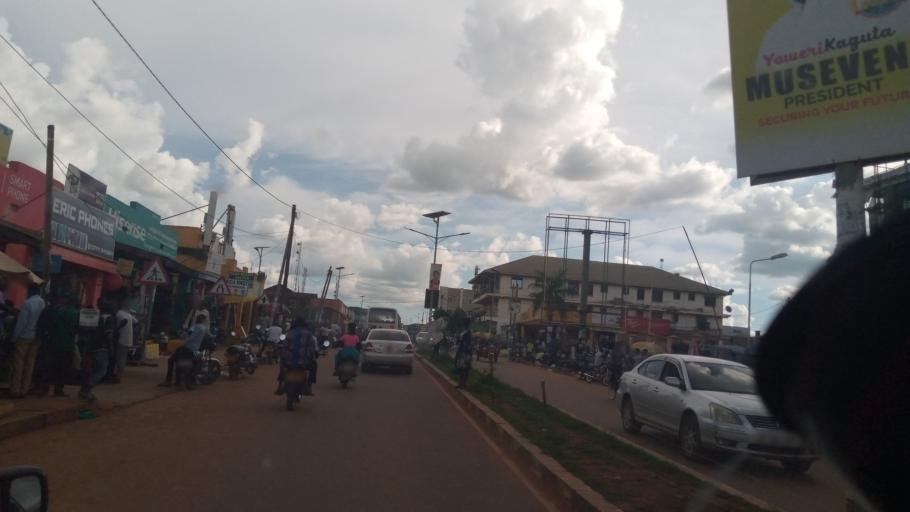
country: UG
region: Northern Region
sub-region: Lira District
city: Lira
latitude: 2.2434
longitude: 32.8974
